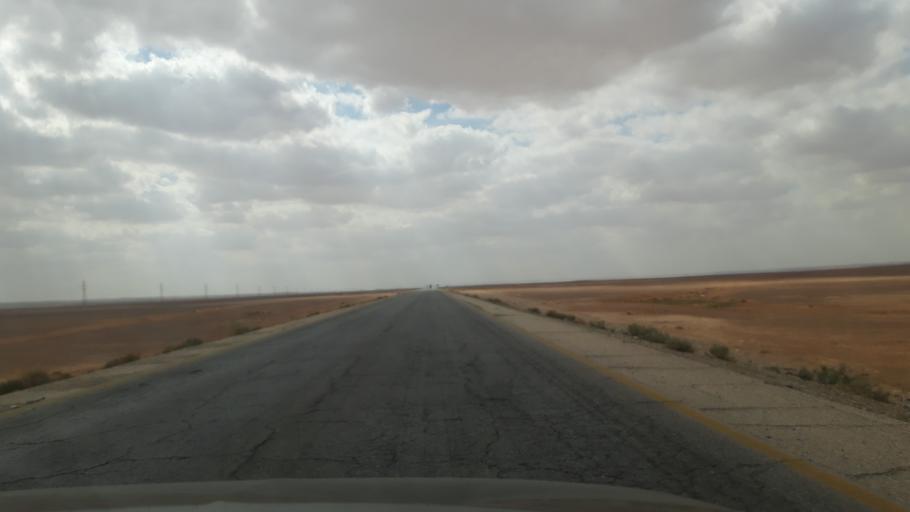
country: JO
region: Amman
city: Sahab
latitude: 31.7477
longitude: 36.4178
